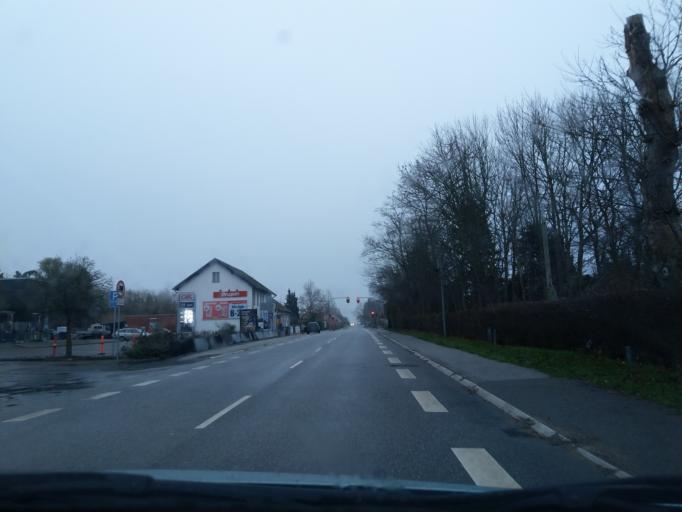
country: DK
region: Zealand
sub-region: Vordingborg Kommune
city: Orslev
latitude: 55.1257
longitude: 11.9503
